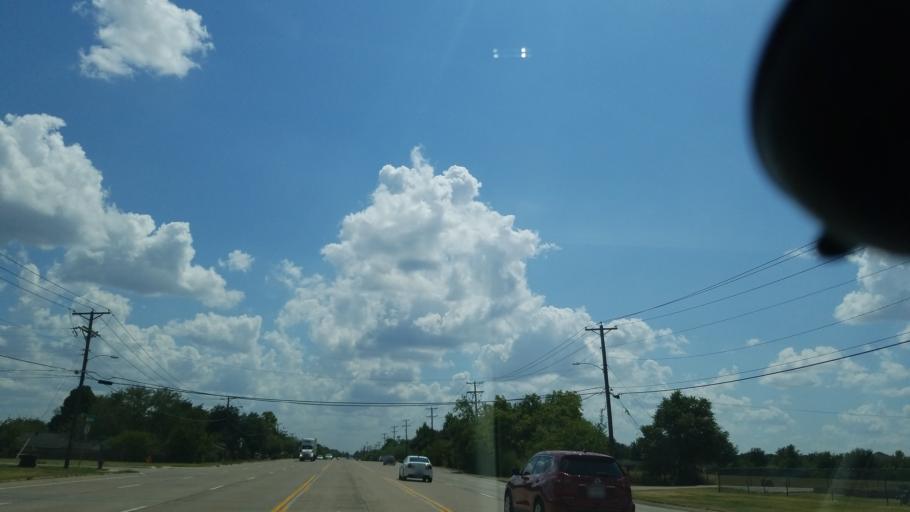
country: US
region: Texas
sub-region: Dallas County
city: Grand Prairie
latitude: 32.7290
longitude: -96.9942
